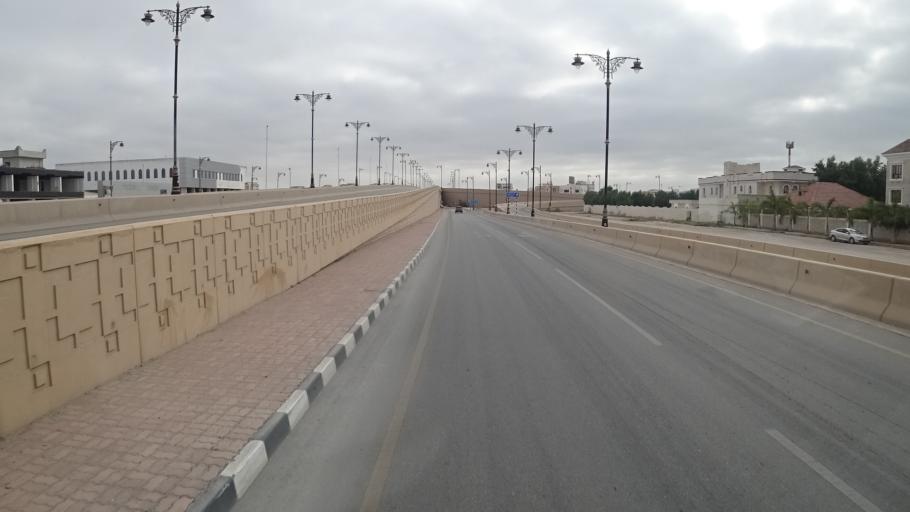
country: OM
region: Zufar
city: Salalah
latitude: 17.0151
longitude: 54.0547
